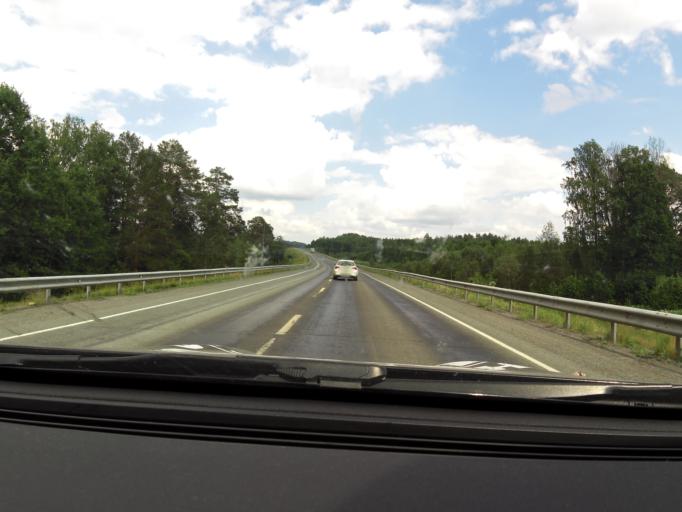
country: RU
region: Sverdlovsk
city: Bisert'
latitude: 56.8335
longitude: 58.8375
